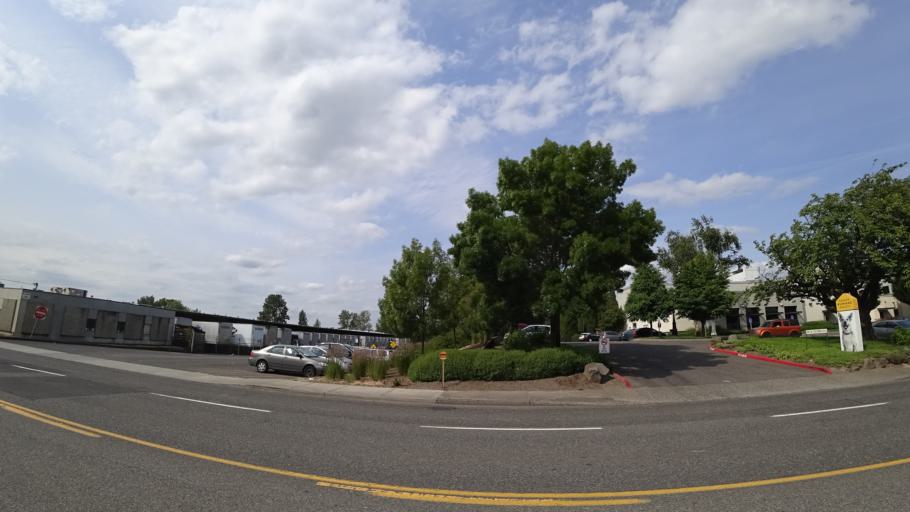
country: US
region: Oregon
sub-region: Multnomah County
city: Portland
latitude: 45.5789
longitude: -122.6537
